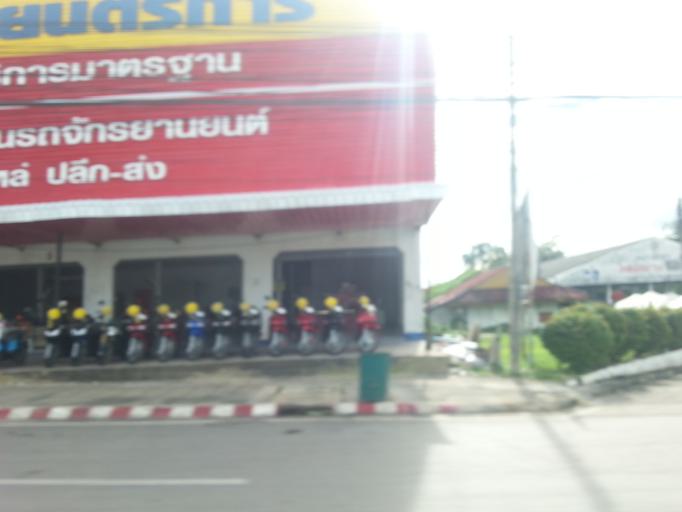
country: TH
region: Krabi
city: Nuea Khlong
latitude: 8.0667
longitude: 99.0017
